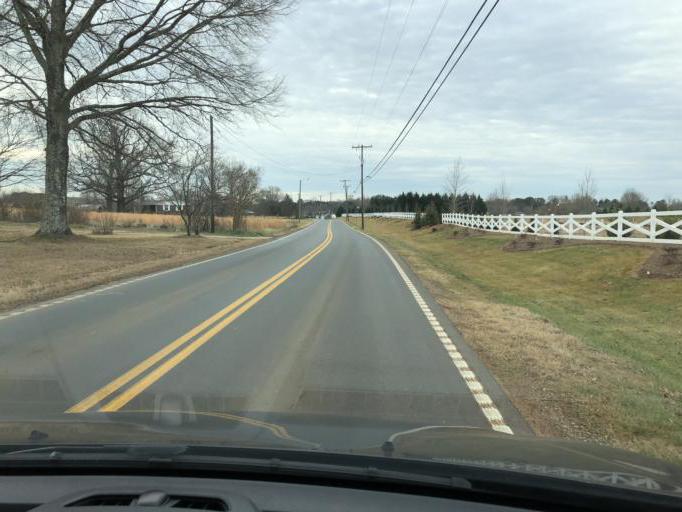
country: US
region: South Carolina
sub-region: Greenville County
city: Greer
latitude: 34.8720
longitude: -82.1996
